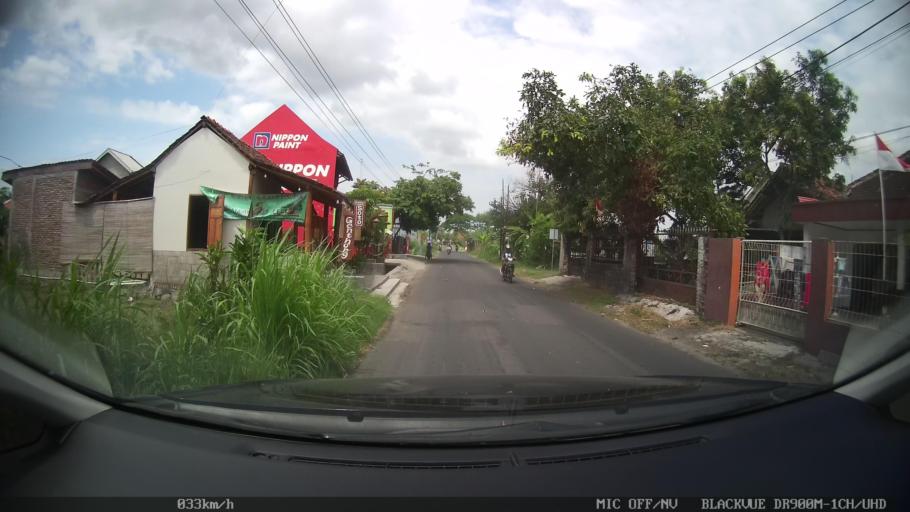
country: ID
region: Daerah Istimewa Yogyakarta
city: Depok
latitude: -7.7922
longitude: 110.4587
